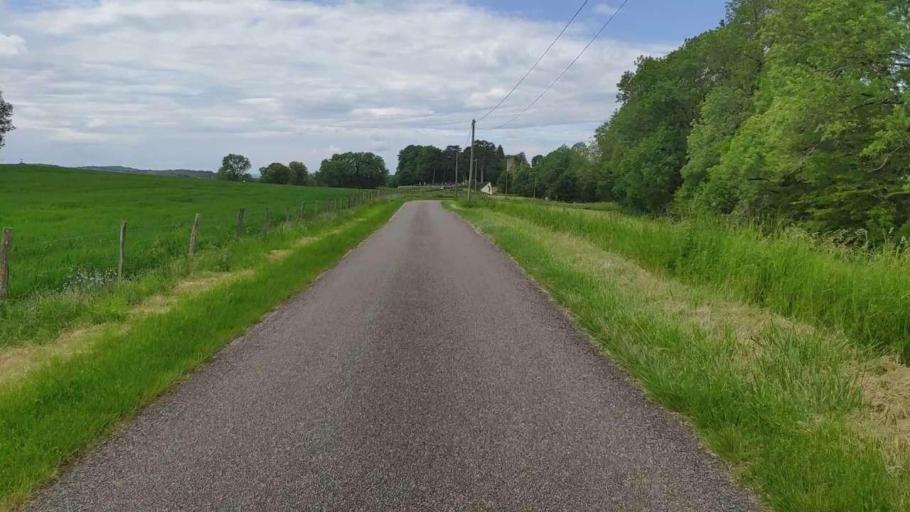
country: FR
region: Franche-Comte
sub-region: Departement du Jura
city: Perrigny
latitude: 46.7574
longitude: 5.6339
